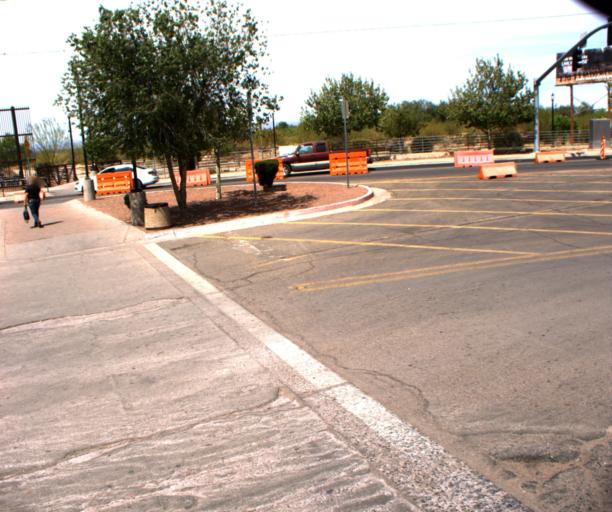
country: MX
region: Sonora
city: Agua Prieta
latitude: 31.3353
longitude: -109.5602
